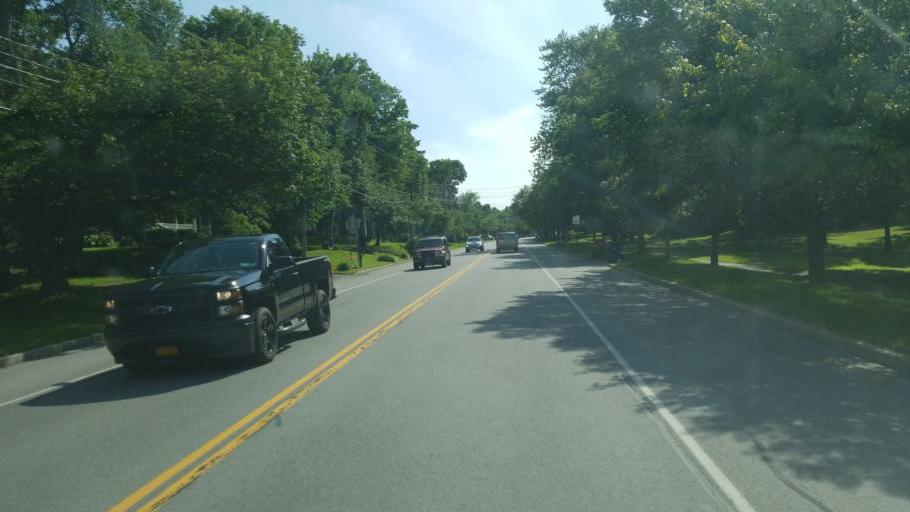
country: US
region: New York
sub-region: Livingston County
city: Lima
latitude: 42.9067
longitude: -77.6071
